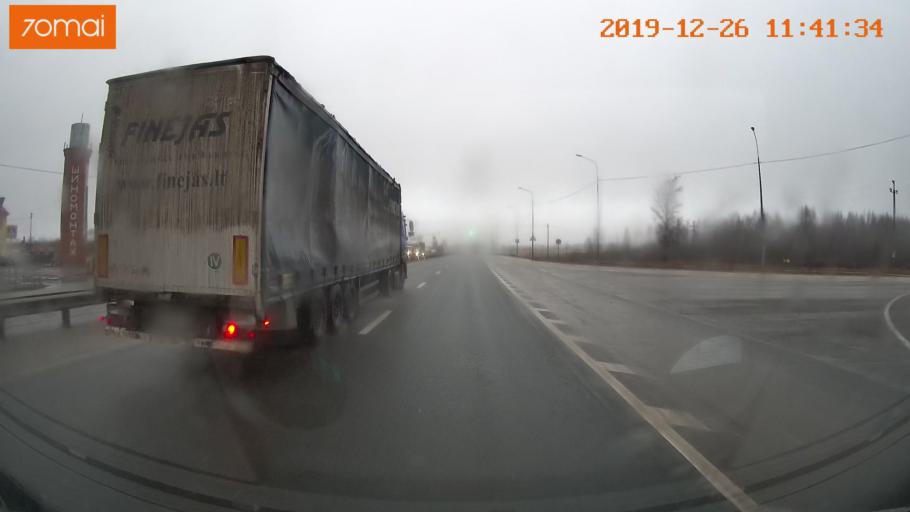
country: RU
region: Vologda
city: Sheksna
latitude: 59.2119
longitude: 38.5404
